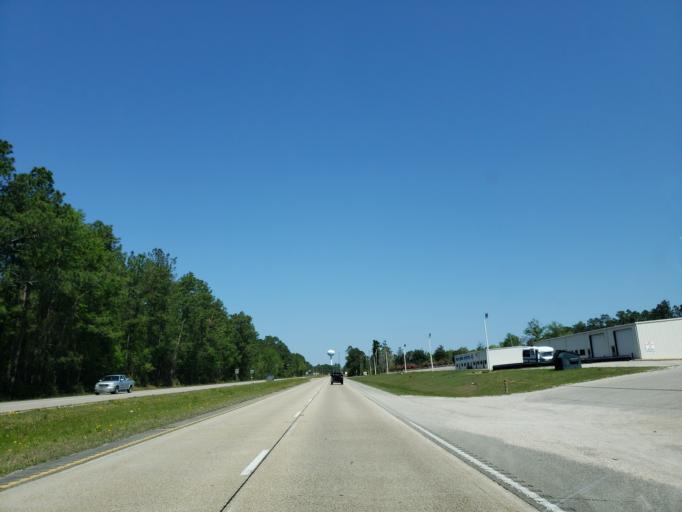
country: US
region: Mississippi
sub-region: Harrison County
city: Saucier
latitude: 30.5781
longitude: -89.1258
